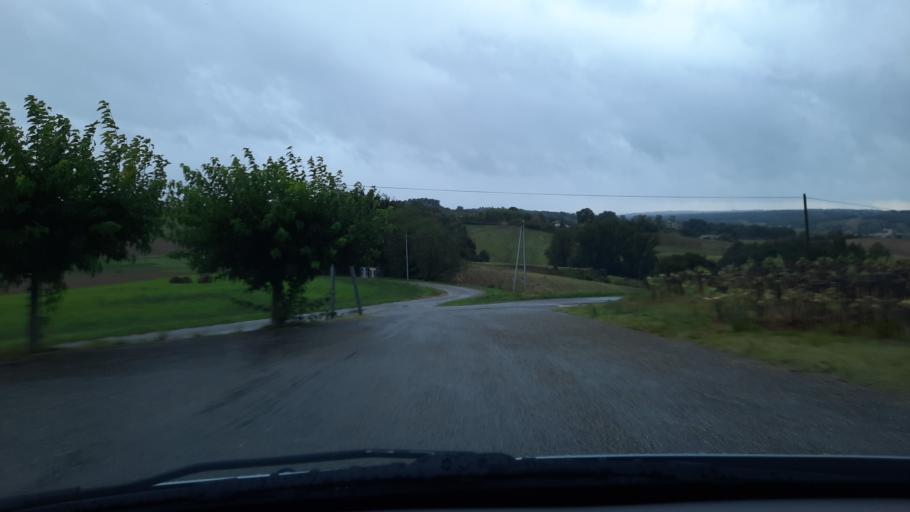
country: FR
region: Midi-Pyrenees
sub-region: Departement du Tarn-et-Garonne
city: Molieres
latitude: 44.1948
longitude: 1.3120
